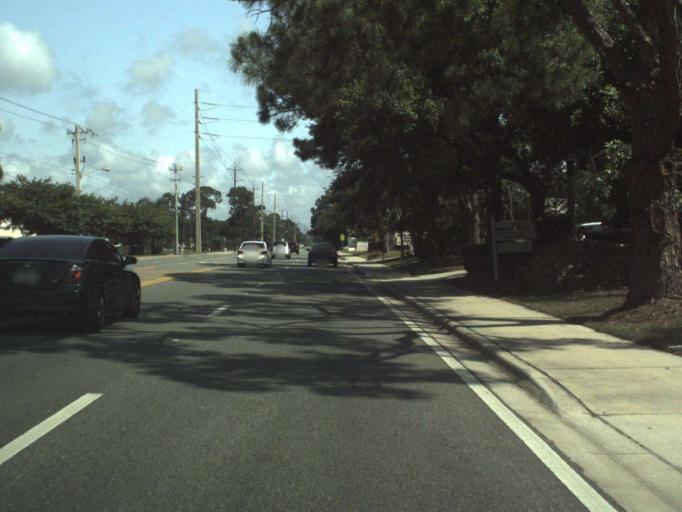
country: US
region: Florida
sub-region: Volusia County
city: Daytona Beach
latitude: 29.2031
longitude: -81.0565
